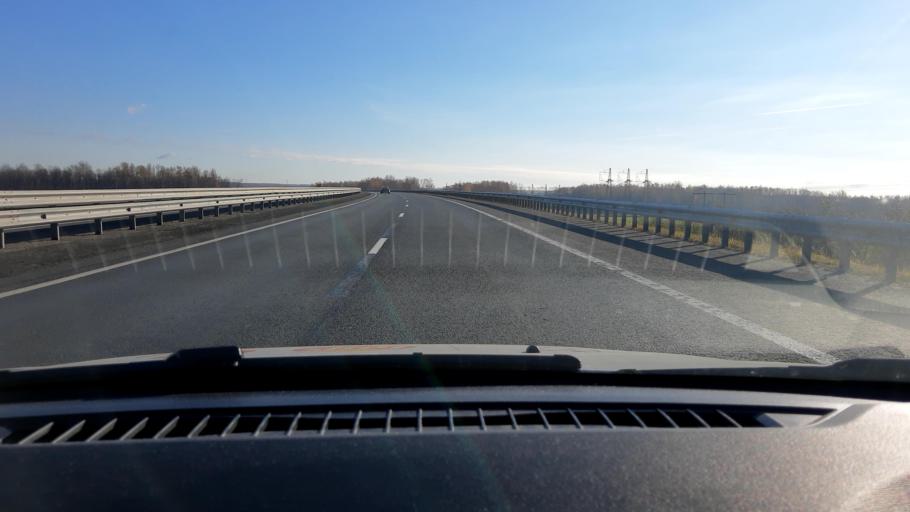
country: RU
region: Nizjnij Novgorod
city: Burevestnik
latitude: 56.1151
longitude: 43.8269
